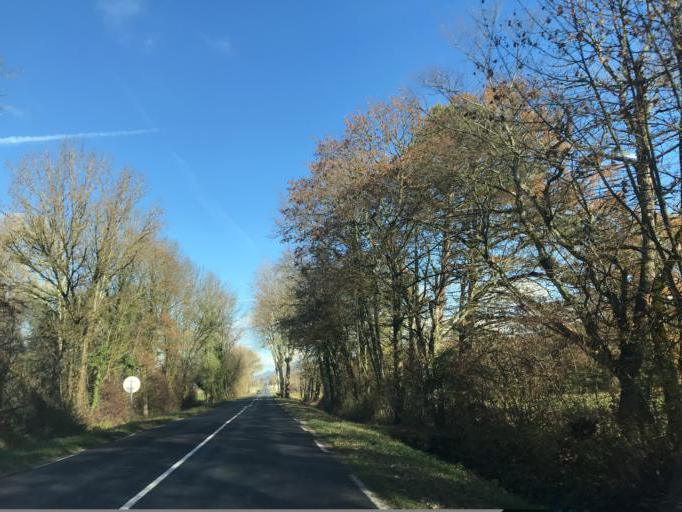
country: FR
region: Rhone-Alpes
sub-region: Departement de l'Ain
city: Ambronay
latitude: 46.0100
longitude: 5.3636
